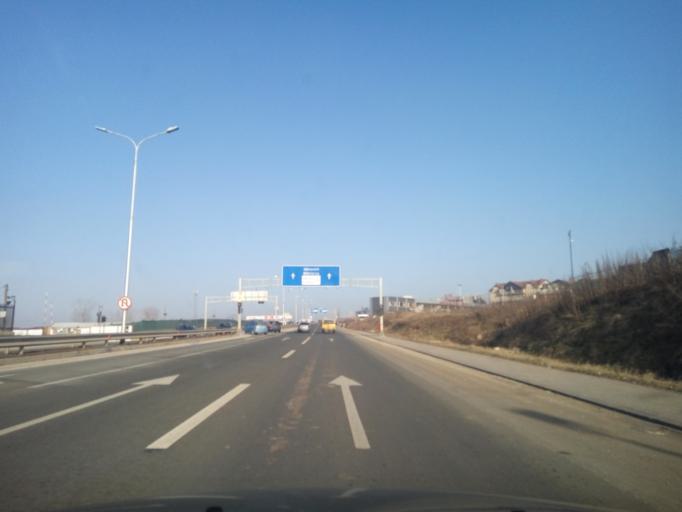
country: XK
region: Pristina
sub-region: Komuna e Prishtines
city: Pristina
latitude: 42.6563
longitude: 21.1394
